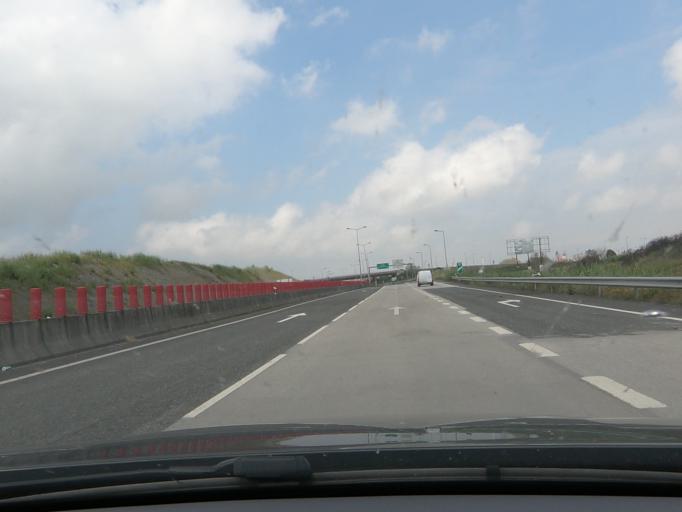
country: PT
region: Leiria
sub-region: Peniche
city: Atouguia da Baleia
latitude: 39.3315
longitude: -9.2531
